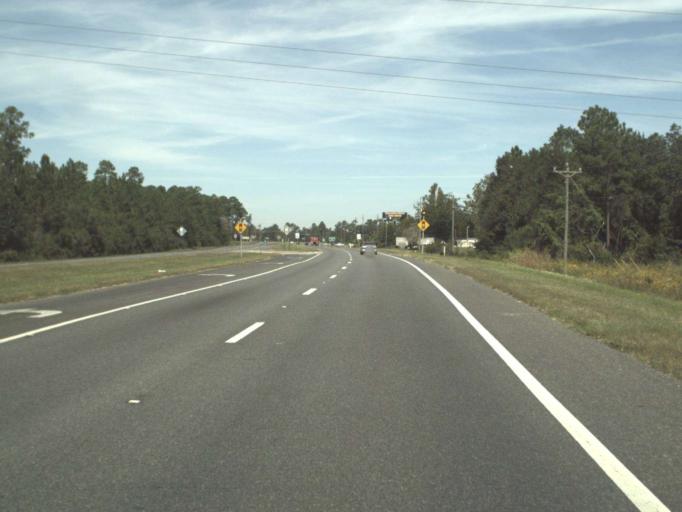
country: US
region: Florida
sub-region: Bay County
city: Lynn Haven
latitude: 30.3175
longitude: -85.6564
